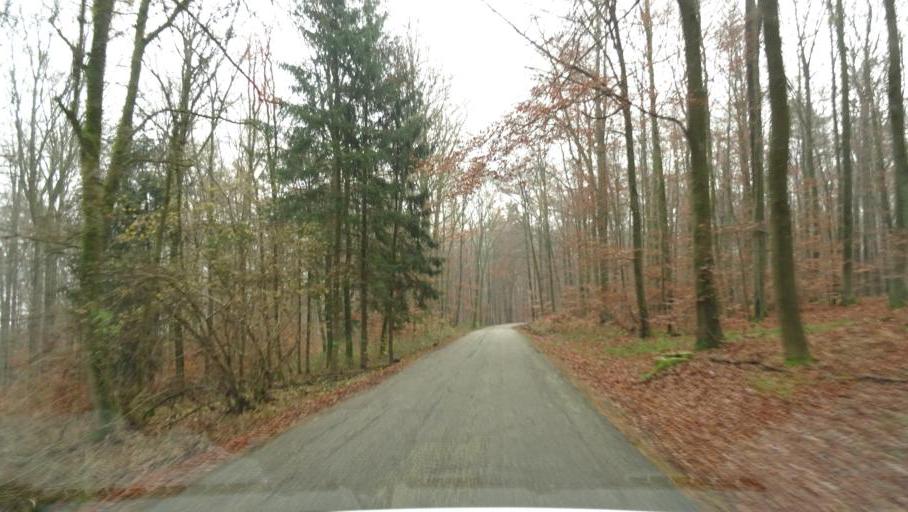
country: DE
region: Baden-Wuerttemberg
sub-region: Karlsruhe Region
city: Huffenhardt
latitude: 49.3205
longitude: 9.0827
